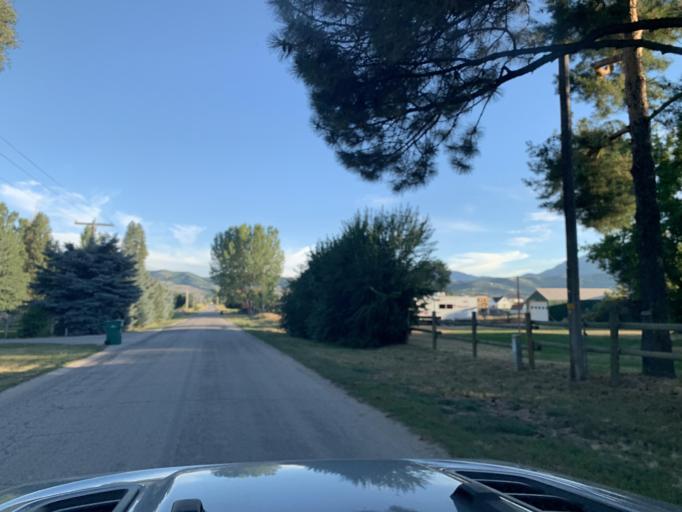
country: US
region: Utah
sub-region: Weber County
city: Wolf Creek
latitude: 41.2781
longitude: -111.7621
